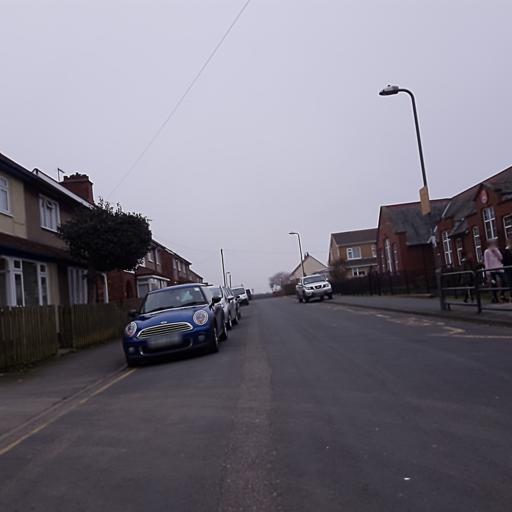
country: GB
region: England
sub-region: North Yorkshire
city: Filey
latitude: 54.2118
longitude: -0.2942
